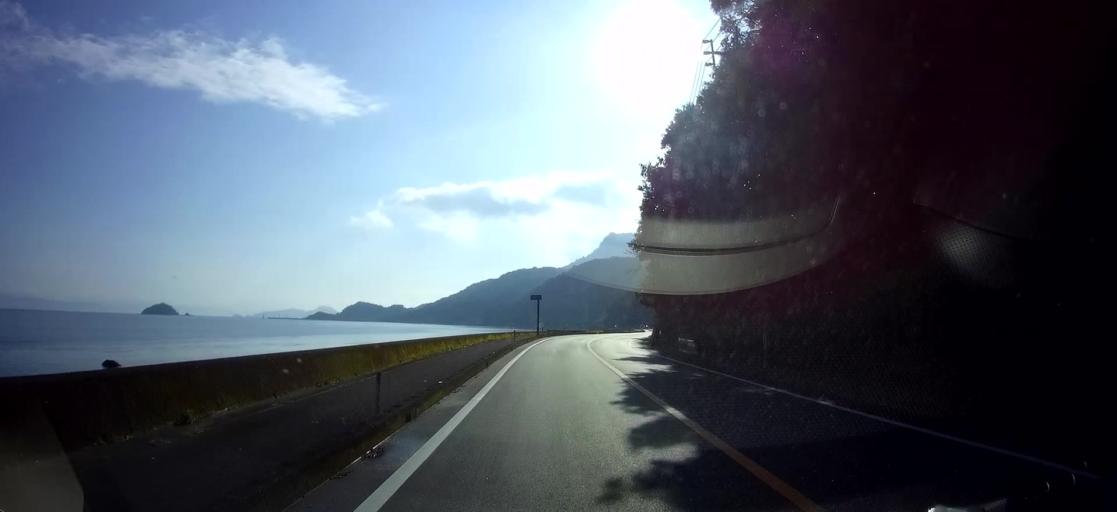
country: JP
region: Kumamoto
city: Yatsushiro
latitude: 32.4908
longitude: 130.4411
